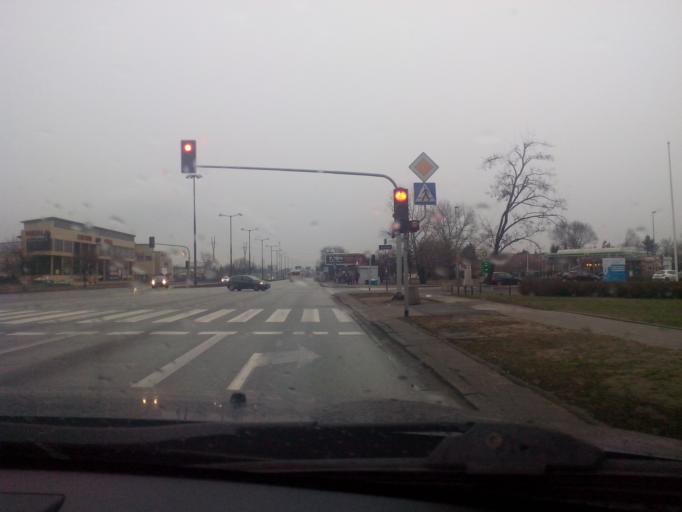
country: PL
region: Masovian Voivodeship
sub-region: Warszawa
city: Bialoleka
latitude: 52.3215
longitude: 20.9715
